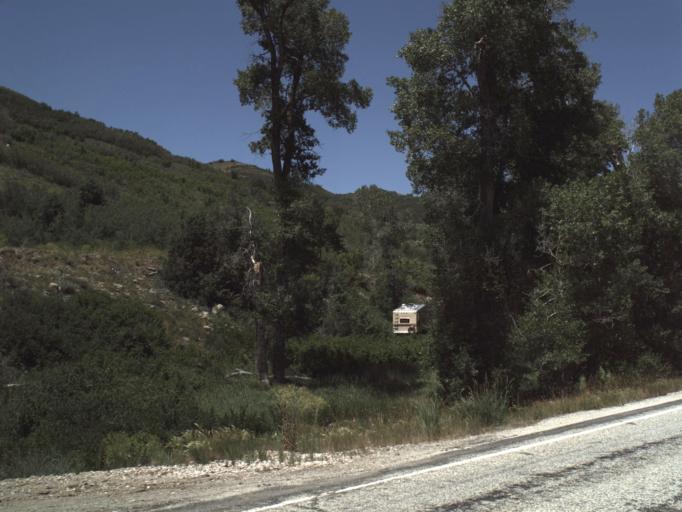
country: US
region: Utah
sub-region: Weber County
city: Wolf Creek
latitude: 41.3618
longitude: -111.5926
